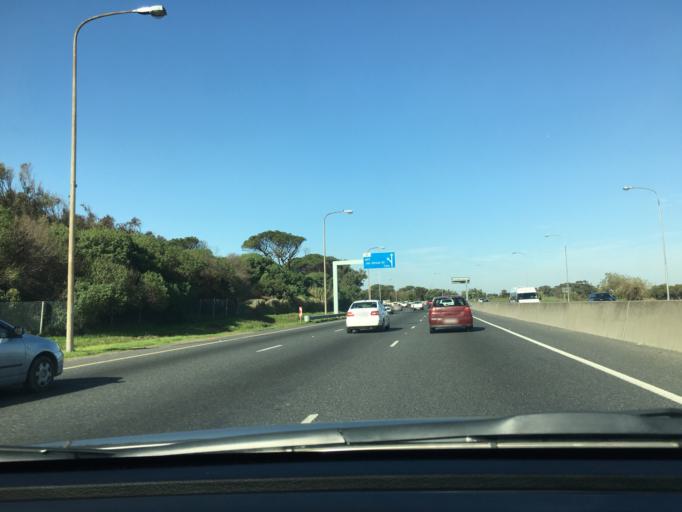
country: ZA
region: Western Cape
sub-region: City of Cape Town
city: Rosebank
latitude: -33.9500
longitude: 18.4919
